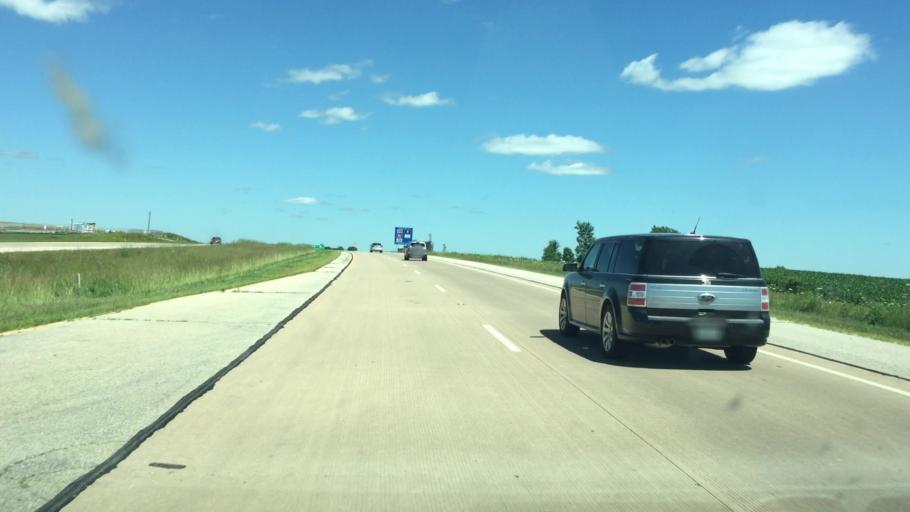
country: US
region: Wisconsin
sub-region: Grant County
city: Platteville
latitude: 42.7107
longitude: -90.4979
